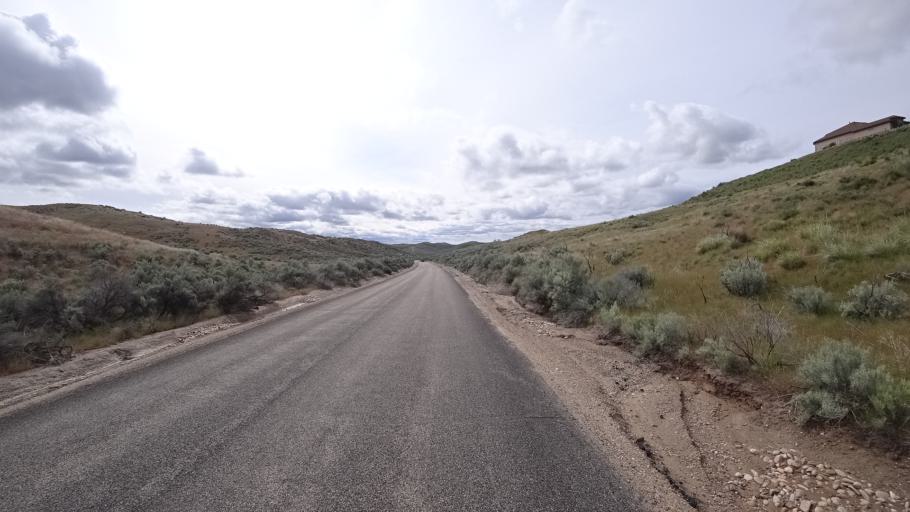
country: US
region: Idaho
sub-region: Ada County
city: Eagle
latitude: 43.7560
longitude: -116.3660
